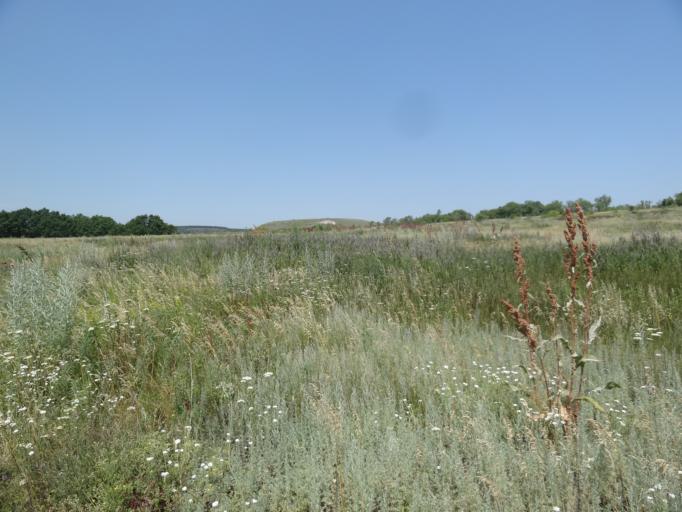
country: RU
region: Saratov
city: Sokolovyy
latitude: 51.4237
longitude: 45.8077
